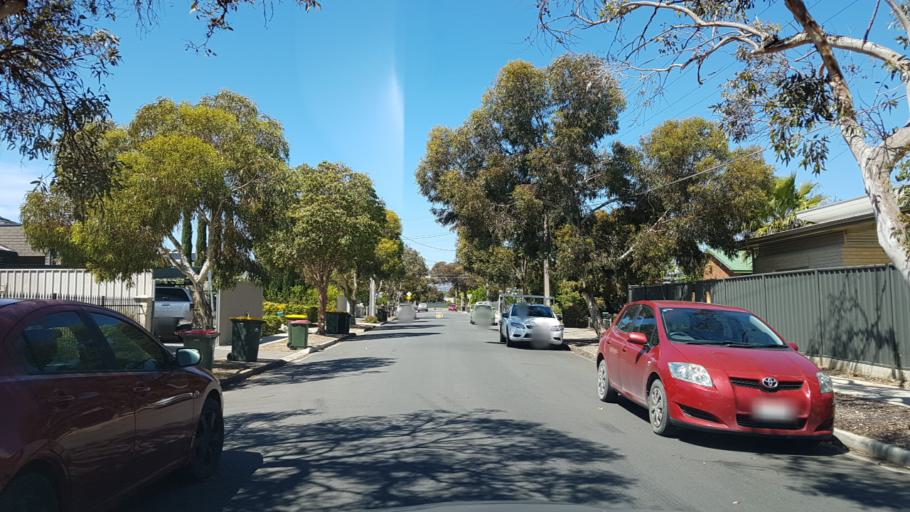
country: AU
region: South Australia
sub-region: Marion
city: Plympton Park
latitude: -34.9786
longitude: 138.5482
